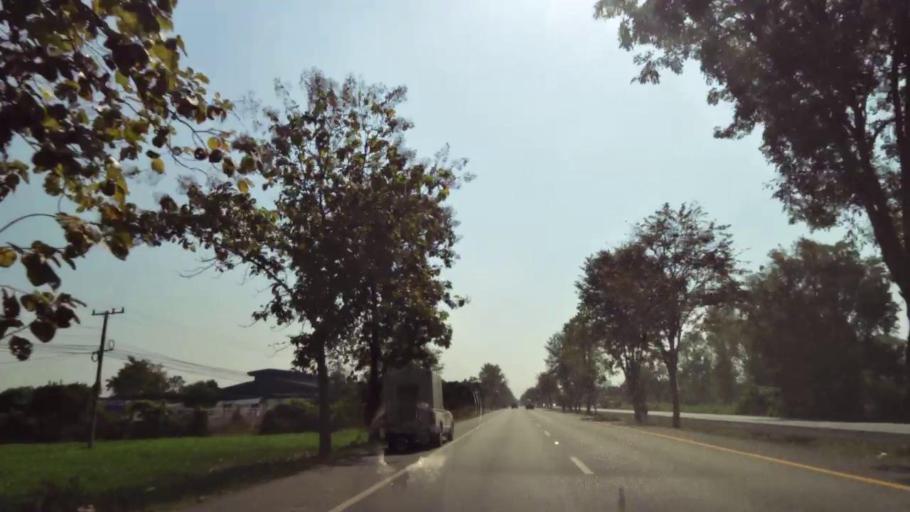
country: TH
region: Phichit
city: Bueng Na Rang
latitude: 16.0799
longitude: 100.1245
